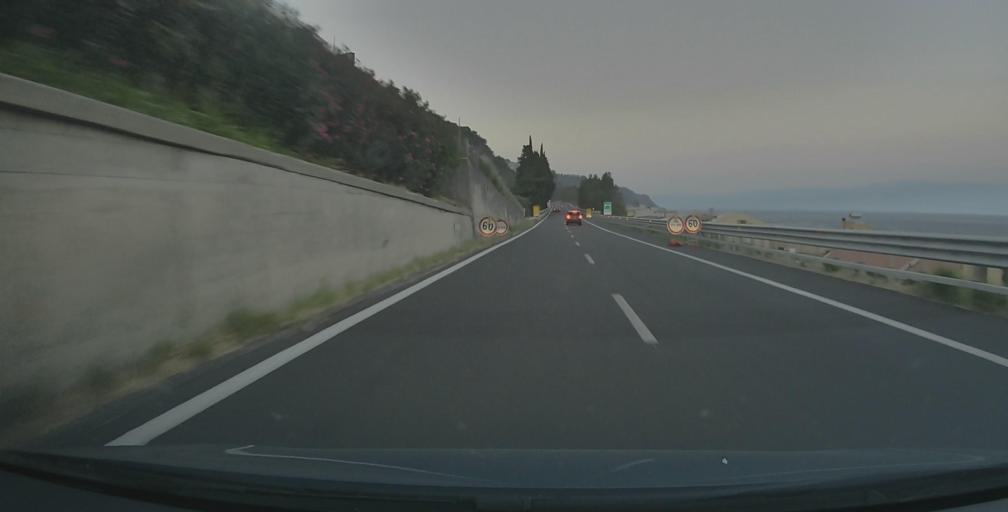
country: IT
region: Sicily
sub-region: Messina
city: Guidomandri Marina
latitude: 38.0324
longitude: 15.4474
